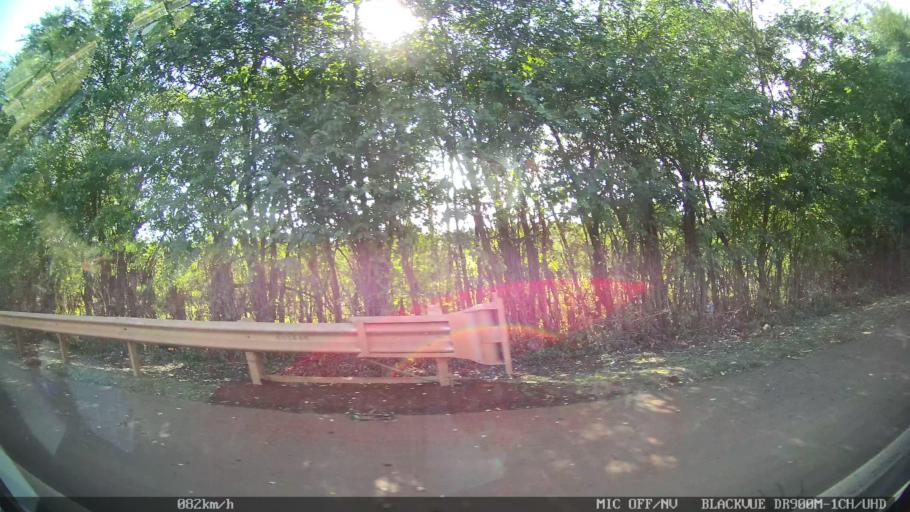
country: BR
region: Sao Paulo
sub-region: Iracemapolis
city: Iracemapolis
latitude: -22.6626
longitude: -47.5310
